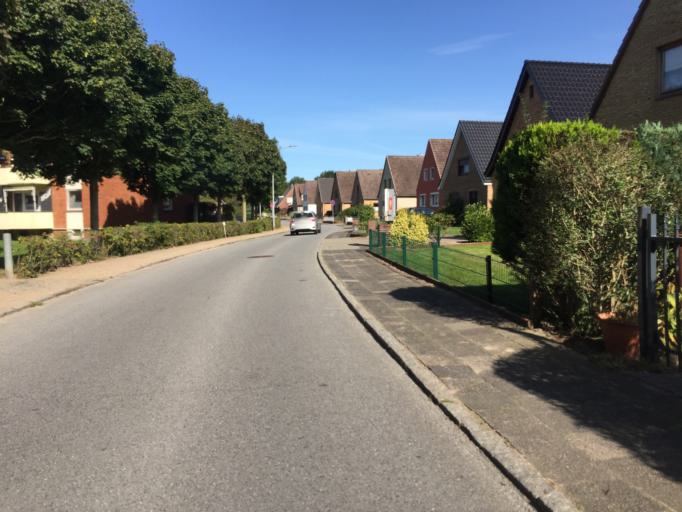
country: DE
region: Schleswig-Holstein
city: Heiligenstedtenerkamp
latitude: 53.9098
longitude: 9.4915
